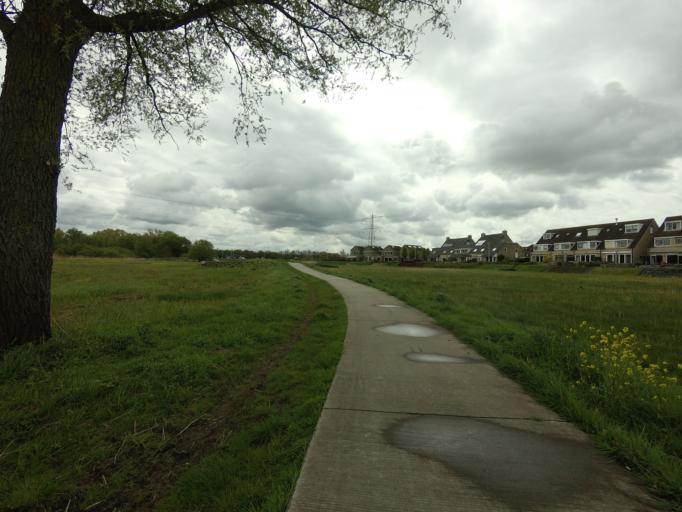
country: NL
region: North Holland
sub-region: Gemeente Naarden
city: Naarden
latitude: 52.3260
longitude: 5.1275
